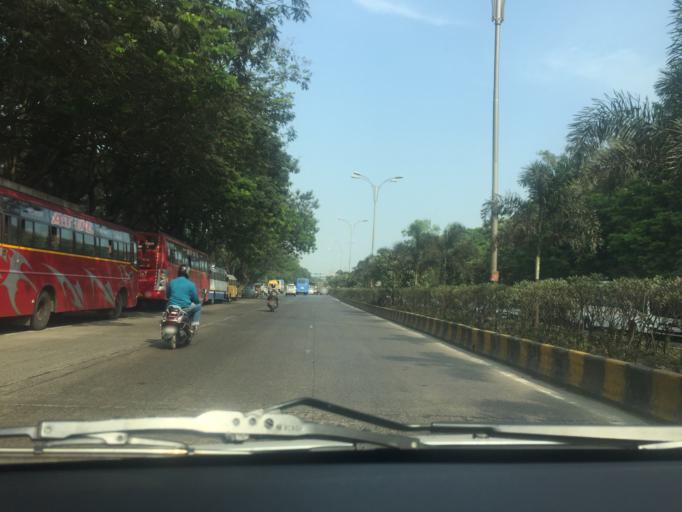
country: IN
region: Maharashtra
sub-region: Thane
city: Airoli
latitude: 19.1537
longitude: 73.0005
